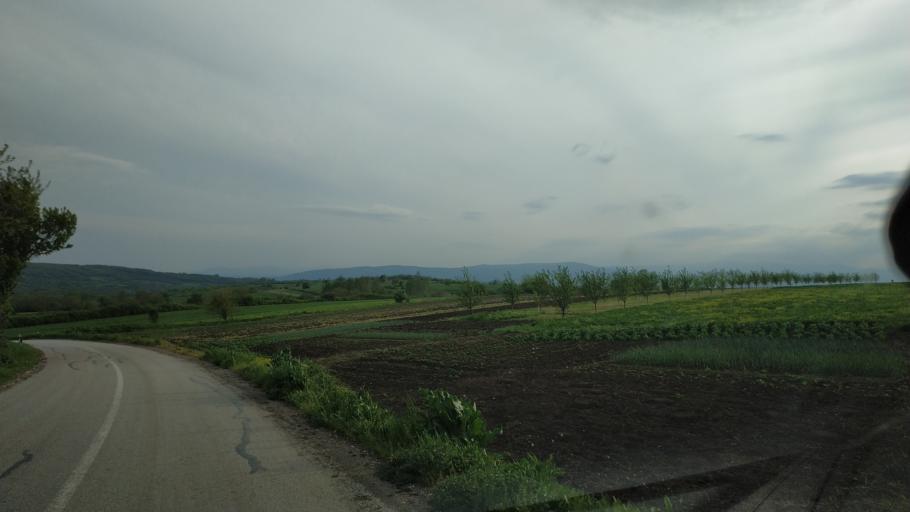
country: RS
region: Central Serbia
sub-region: Zajecarski Okrug
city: Soko Banja
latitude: 43.5248
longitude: 21.8483
